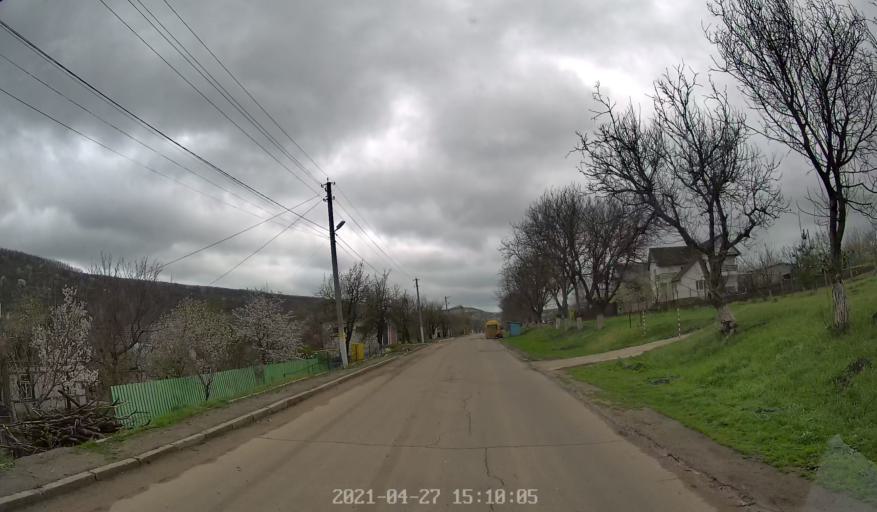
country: MD
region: Chisinau
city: Vadul lui Voda
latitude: 47.0440
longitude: 29.0334
